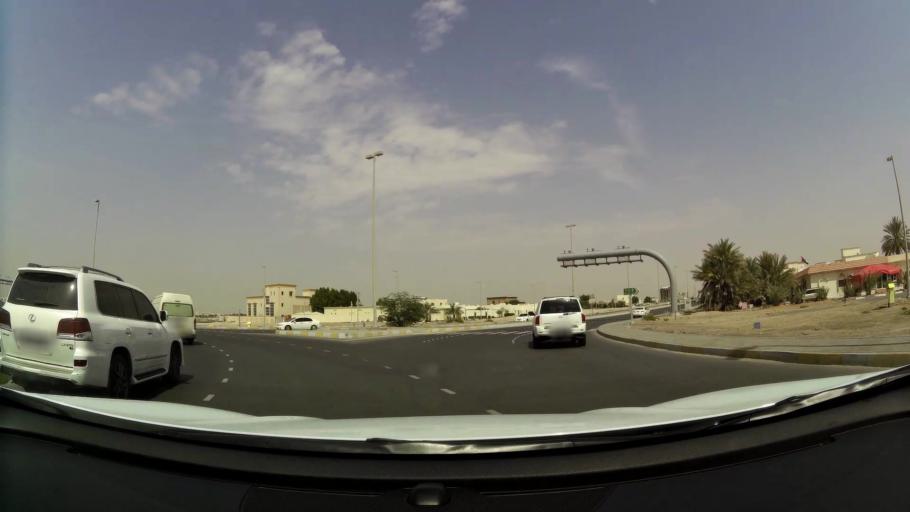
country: AE
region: Abu Dhabi
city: Abu Dhabi
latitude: 24.3011
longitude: 54.6346
